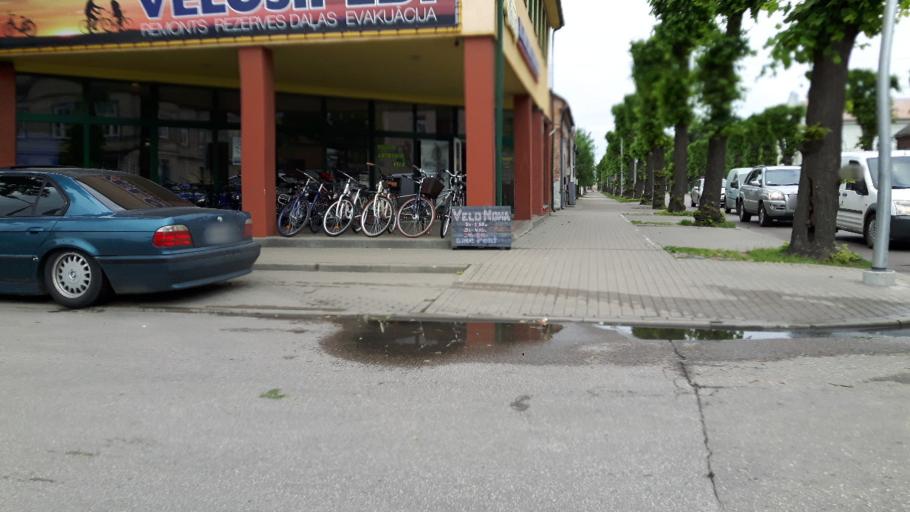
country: LV
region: Liepaja
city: Liepaja
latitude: 56.5181
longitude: 21.0103
